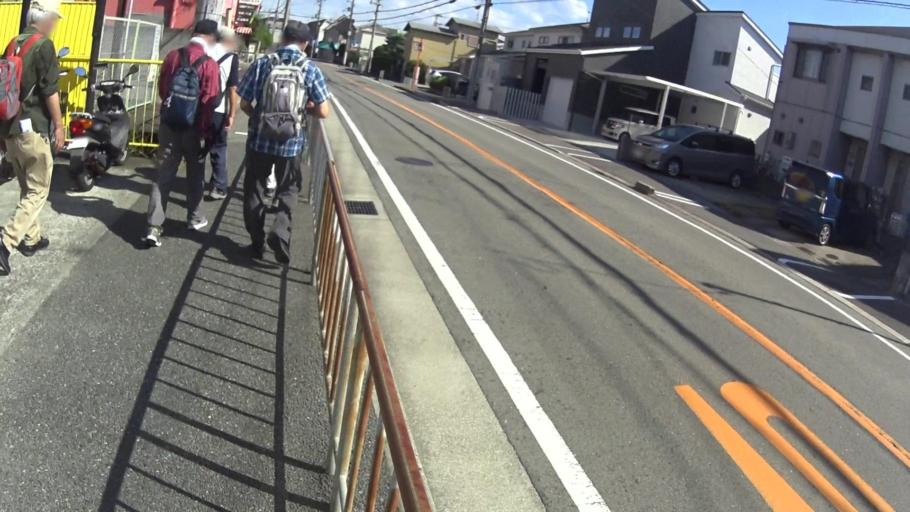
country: JP
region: Ehime
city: Kihoku-cho
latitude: 33.3732
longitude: 132.8037
